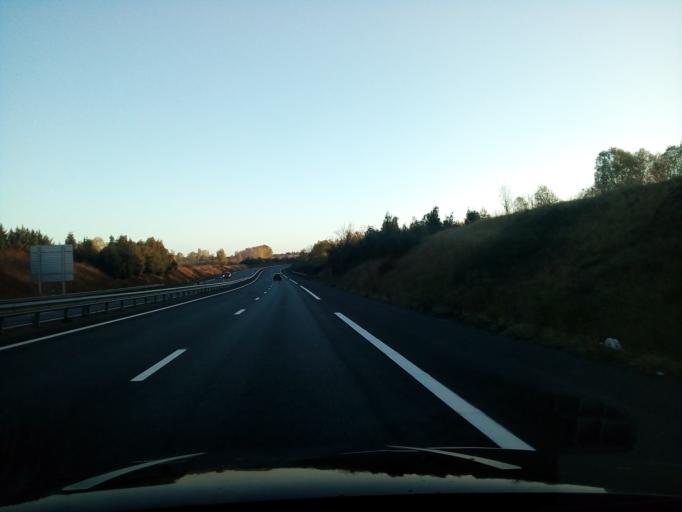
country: FR
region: Poitou-Charentes
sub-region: Departement de la Charente
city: Roullet-Saint-Estephe
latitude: 45.5842
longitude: 0.0437
